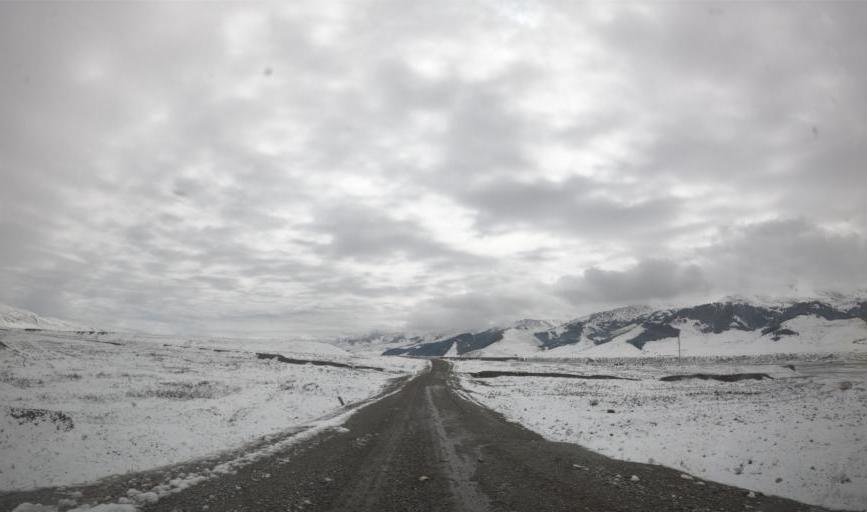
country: KG
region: Naryn
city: Naryn
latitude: 41.2358
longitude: 76.2356
